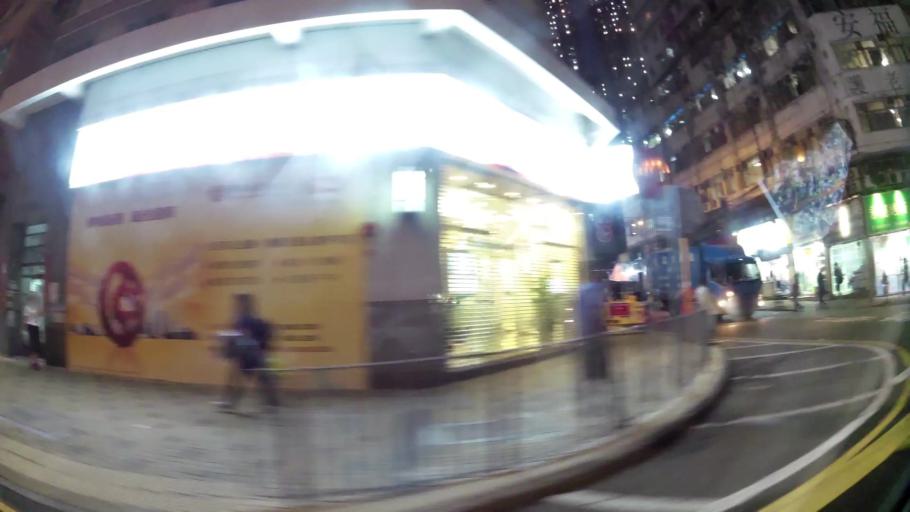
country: HK
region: Tsuen Wan
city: Tsuen Wan
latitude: 22.3684
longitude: 114.1394
